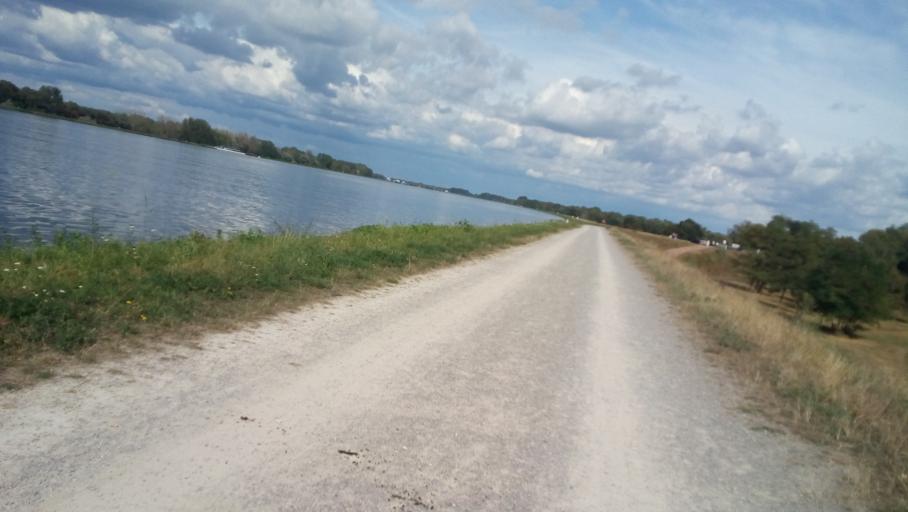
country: DE
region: Baden-Wuerttemberg
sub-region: Karlsruhe Region
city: Hugelsheim
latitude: 48.7959
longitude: 8.0814
